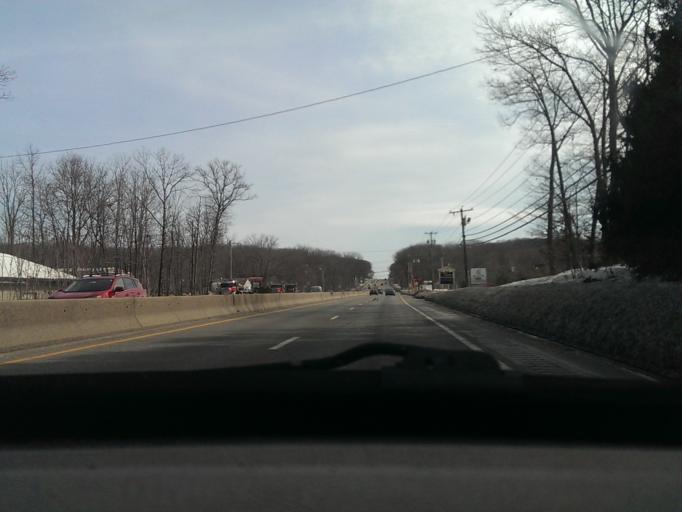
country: US
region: Massachusetts
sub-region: Worcester County
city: Millbury
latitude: 42.1779
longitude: -71.7588
